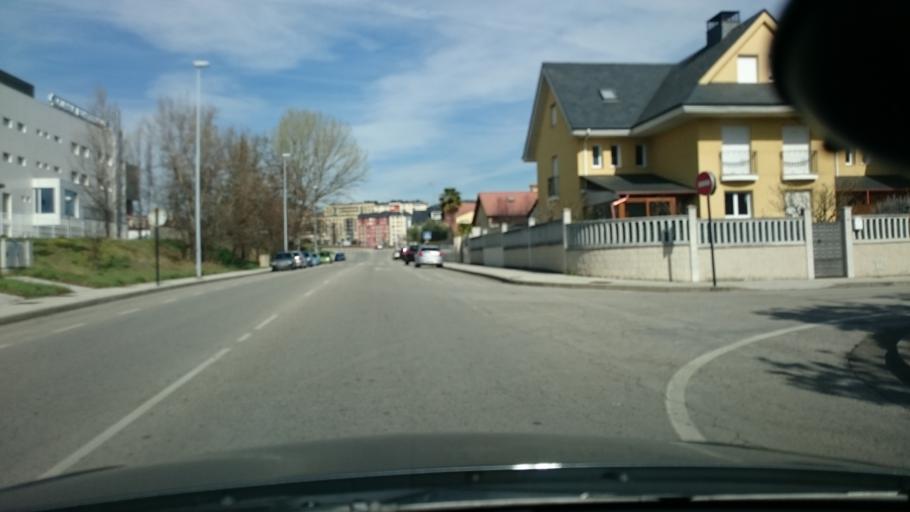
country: ES
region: Castille and Leon
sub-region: Provincia de Leon
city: Ponferrada
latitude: 42.5523
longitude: -6.6119
